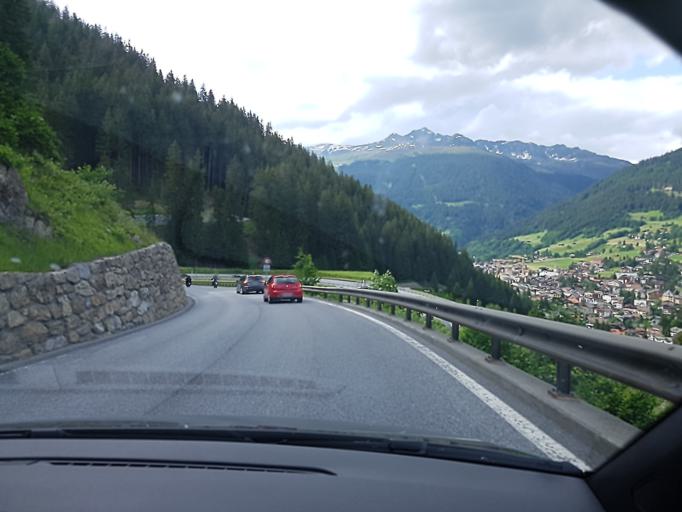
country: CH
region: Grisons
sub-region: Praettigau/Davos District
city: Klosters Serneus
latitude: 46.8584
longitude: 9.8793
